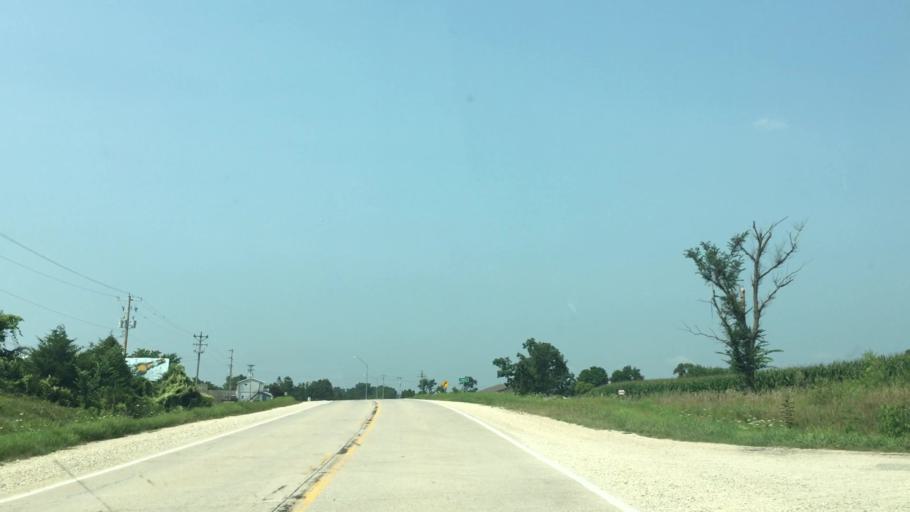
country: US
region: Iowa
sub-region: Fayette County
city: West Union
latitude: 43.1162
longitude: -91.8692
